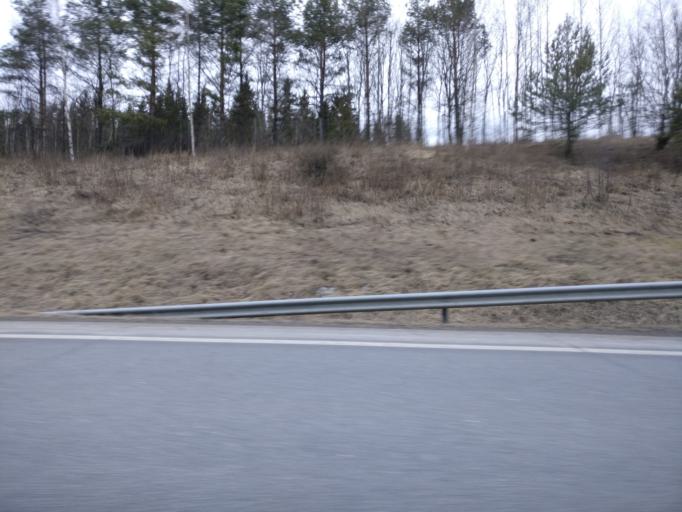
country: FI
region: Pirkanmaa
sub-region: Tampere
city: Tampere
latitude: 61.4627
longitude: 23.7753
